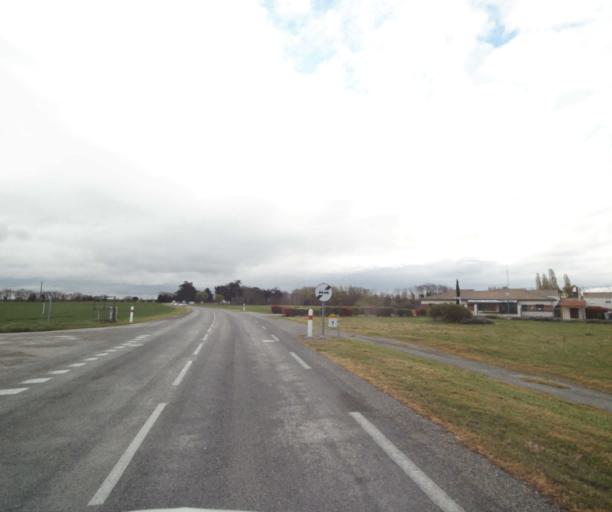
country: FR
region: Midi-Pyrenees
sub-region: Departement de l'Ariege
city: Saverdun
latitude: 43.2310
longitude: 1.5944
